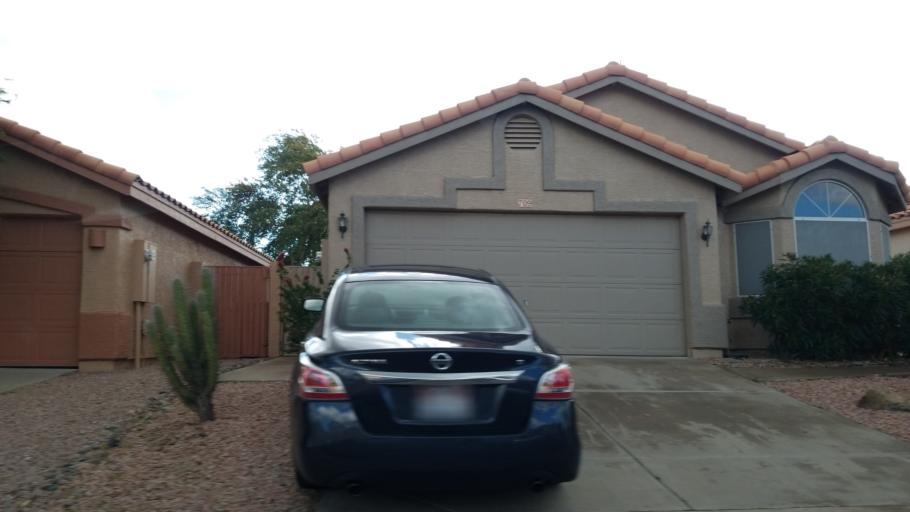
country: US
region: Arizona
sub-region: Maricopa County
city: Laveen
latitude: 33.2941
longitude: -112.0660
